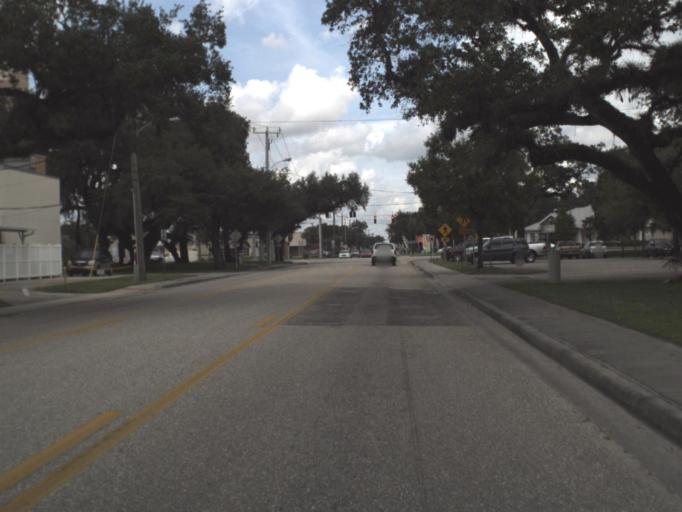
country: US
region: Florida
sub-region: Hendry County
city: LaBelle
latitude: 26.7606
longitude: -81.4374
